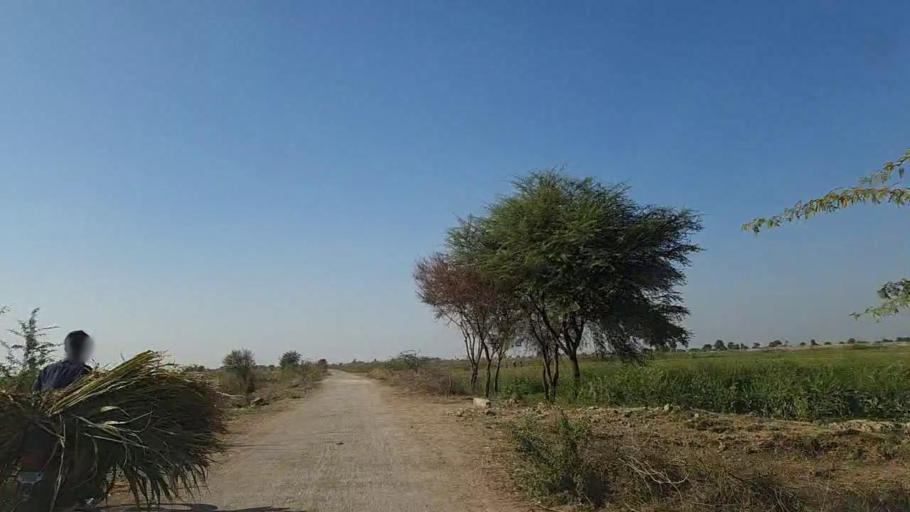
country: PK
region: Sindh
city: Samaro
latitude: 25.3672
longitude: 69.3820
